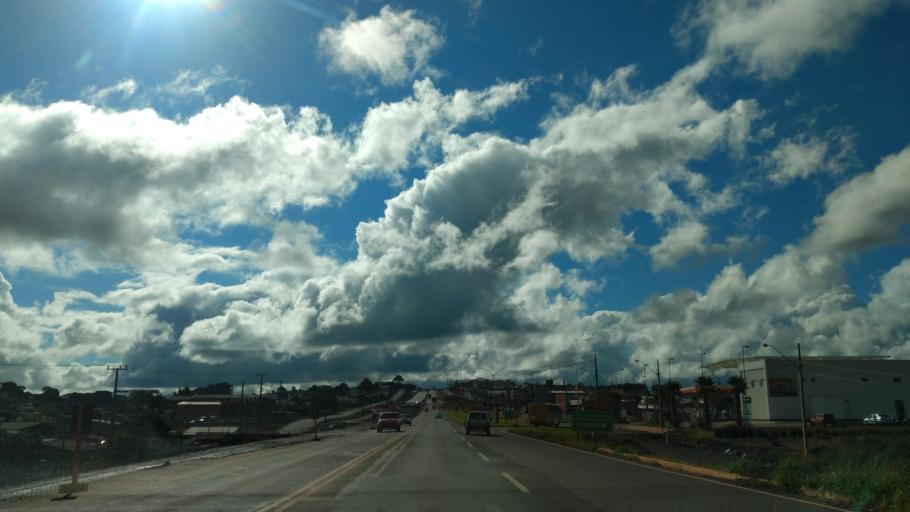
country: BR
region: Parana
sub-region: Guarapuava
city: Guarapuava
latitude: -25.3536
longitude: -51.4850
